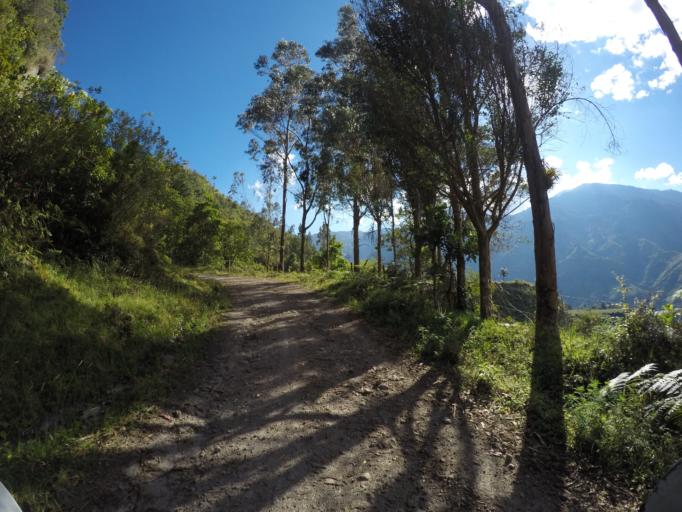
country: CO
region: Tolima
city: Cajamarca
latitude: 4.4991
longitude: -75.3967
